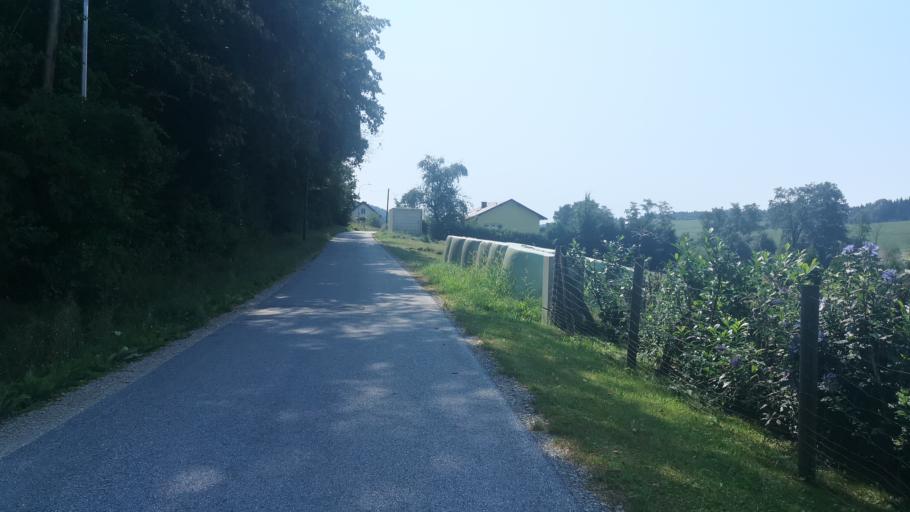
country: AT
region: Styria
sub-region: Politischer Bezirk Deutschlandsberg
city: Lannach
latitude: 46.9345
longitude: 15.3426
